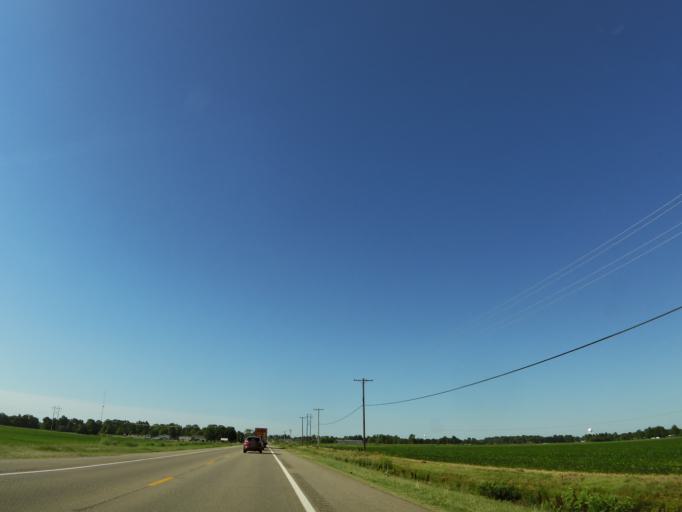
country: US
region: Arkansas
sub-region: Clay County
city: Corning
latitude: 36.4319
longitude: -90.5860
